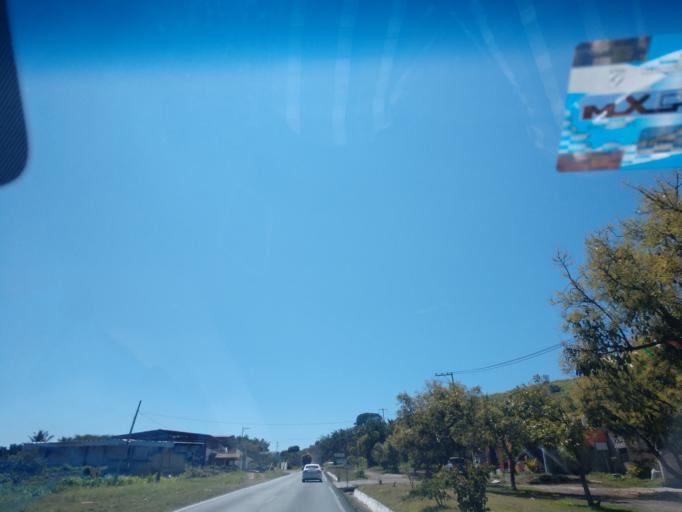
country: MX
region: Nayarit
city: Xalisco
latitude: 21.4118
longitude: -104.8972
